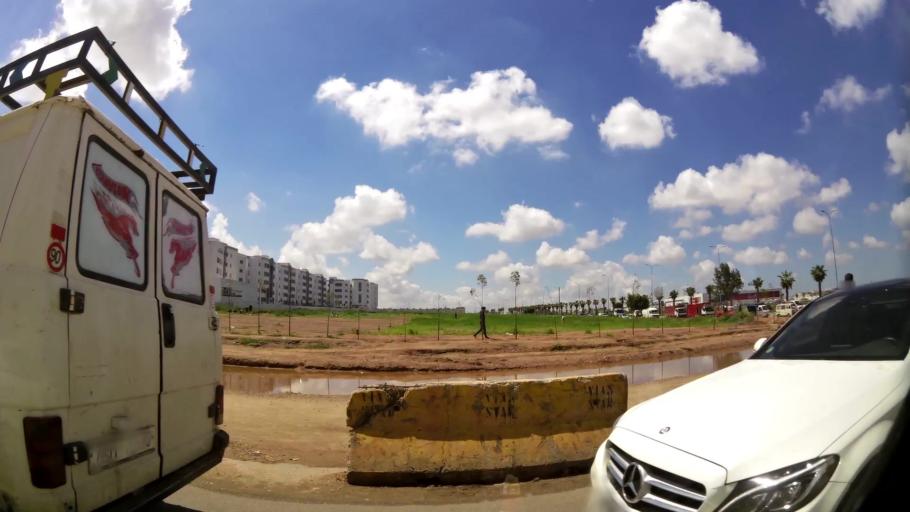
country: MA
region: Grand Casablanca
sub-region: Mediouna
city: Tit Mellil
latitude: 33.5466
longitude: -7.5455
